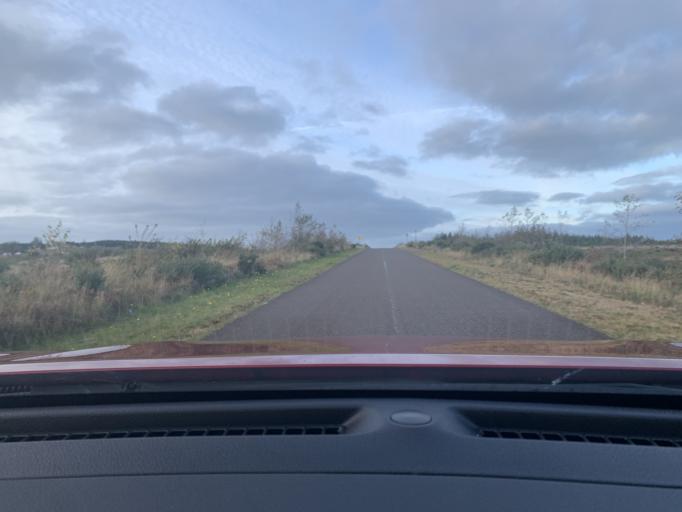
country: IE
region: Connaught
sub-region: Roscommon
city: Ballaghaderreen
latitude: 53.9204
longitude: -8.5916
